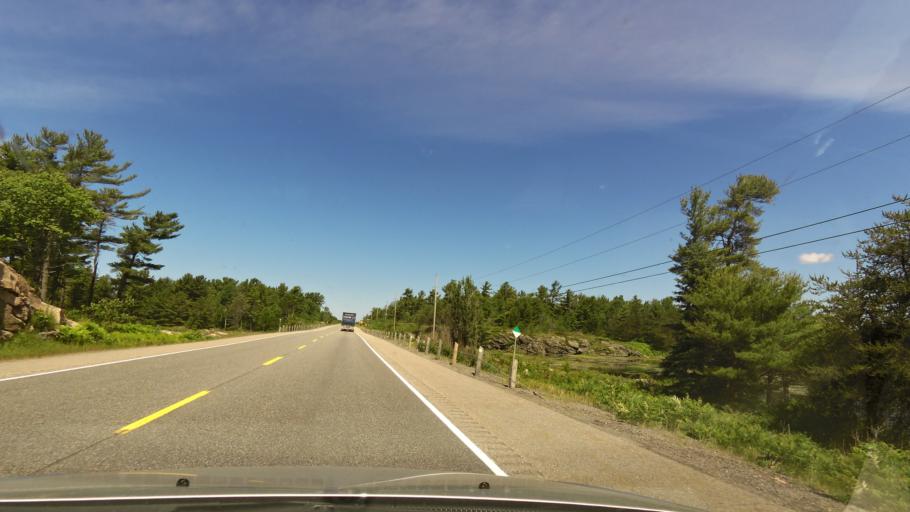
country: CA
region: Ontario
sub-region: Parry Sound District
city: Parry Sound
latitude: 45.6740
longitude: -80.4338
